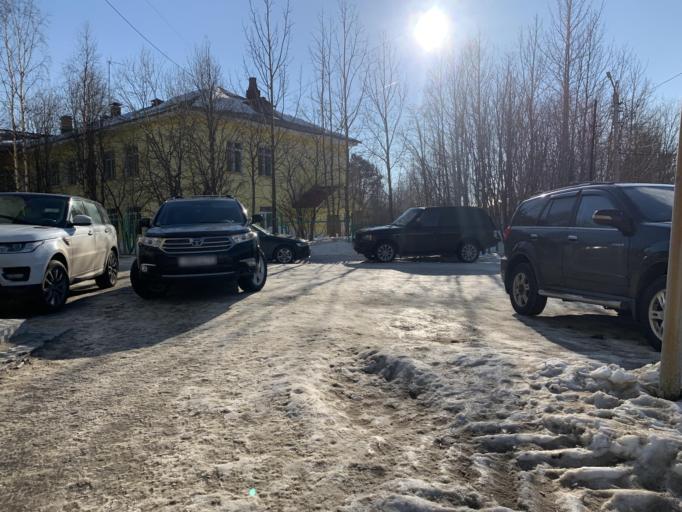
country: RU
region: Murmansk
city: Monchegorsk
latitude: 67.9383
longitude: 32.9396
